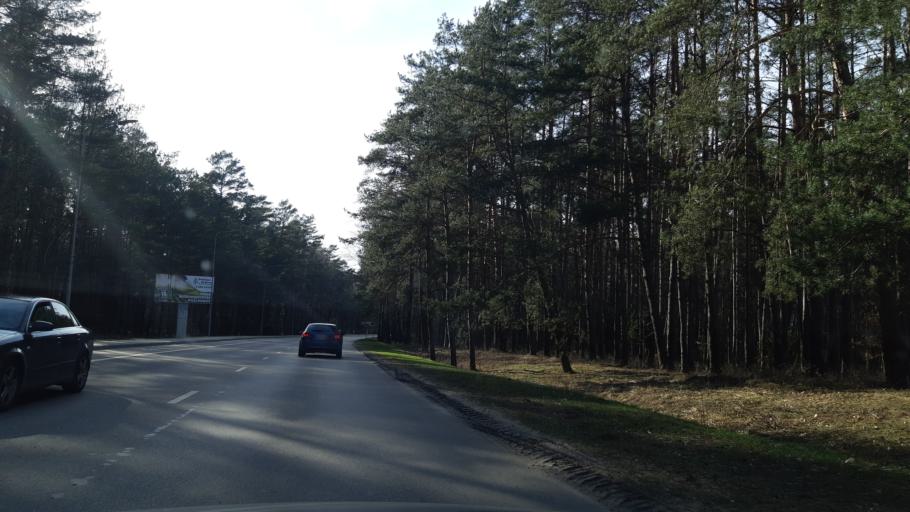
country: LT
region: Alytaus apskritis
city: Druskininkai
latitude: 54.0047
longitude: 24.0126
